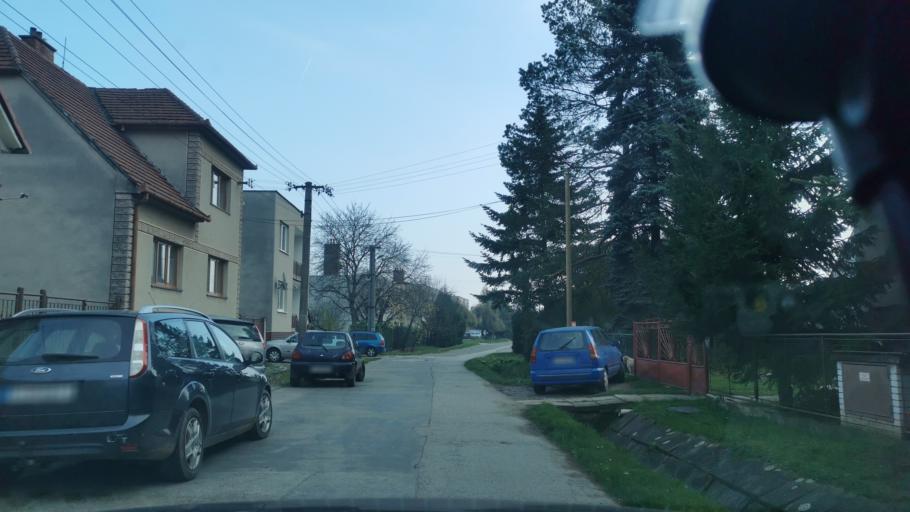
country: SK
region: Trnavsky
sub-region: Okres Skalica
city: Skalica
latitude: 48.7674
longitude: 17.2800
